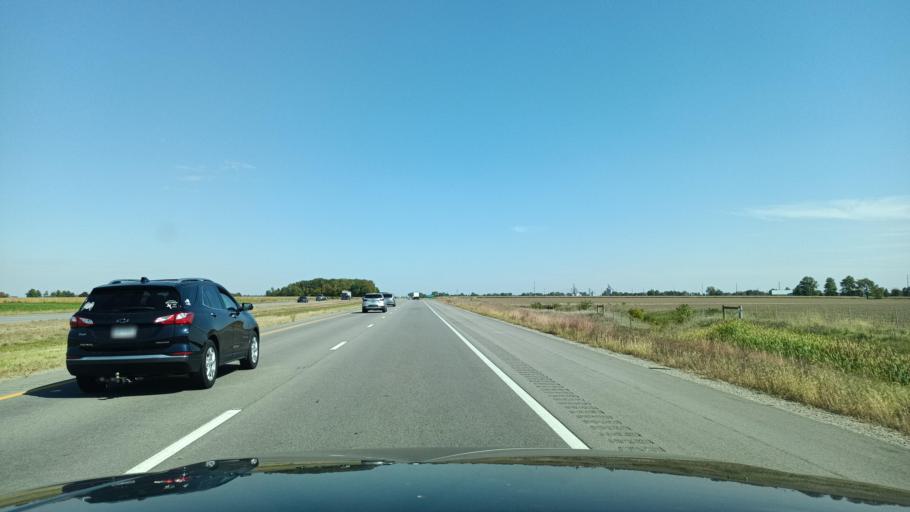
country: US
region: Ohio
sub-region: Henry County
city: Napoleon
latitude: 41.3493
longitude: -84.2435
